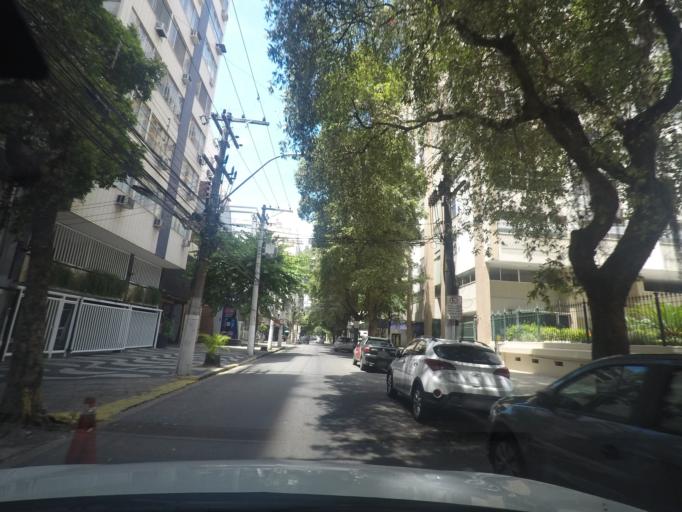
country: BR
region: Rio de Janeiro
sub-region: Niteroi
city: Niteroi
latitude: -22.9057
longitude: -43.1111
